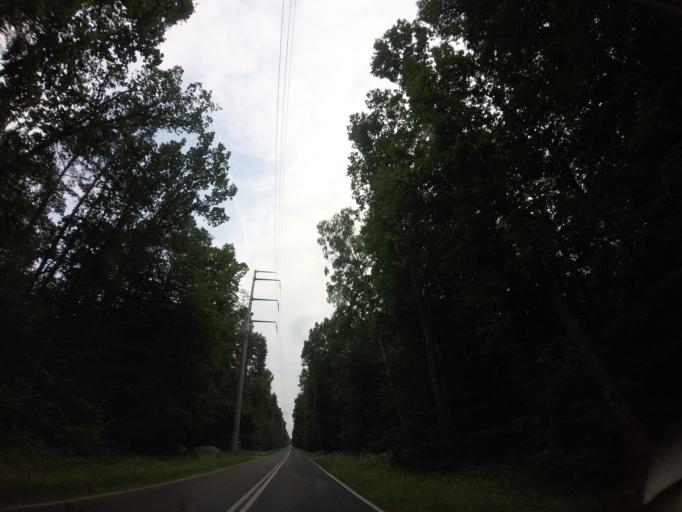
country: PL
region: West Pomeranian Voivodeship
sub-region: Powiat drawski
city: Wierzchowo
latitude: 53.4113
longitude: 16.1964
